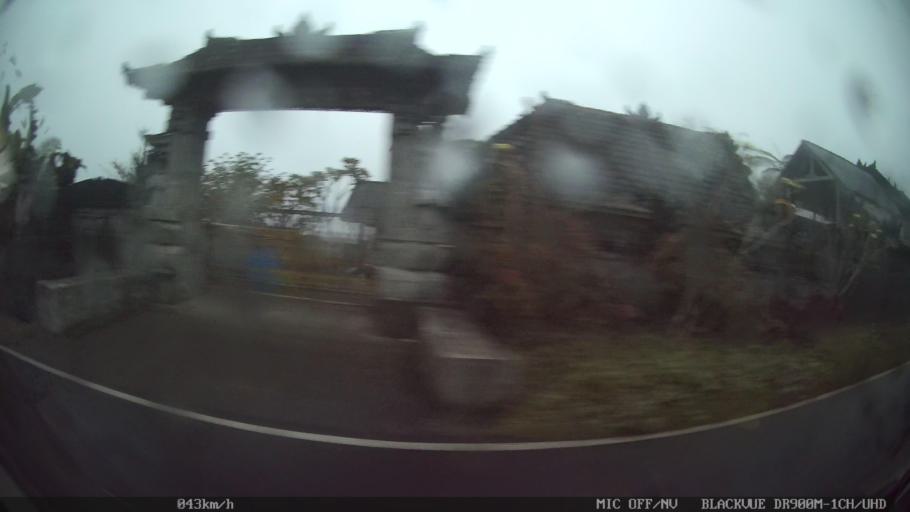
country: ID
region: Bali
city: Banjar Taro Kelod
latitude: -8.3407
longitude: 115.2815
